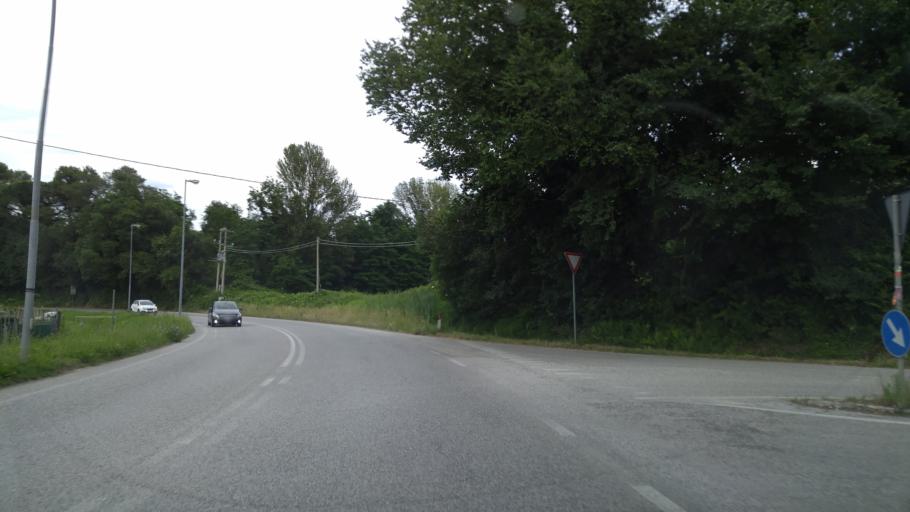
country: IT
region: The Marches
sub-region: Provincia di Pesaro e Urbino
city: Pesaro
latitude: 43.8889
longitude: 12.9193
